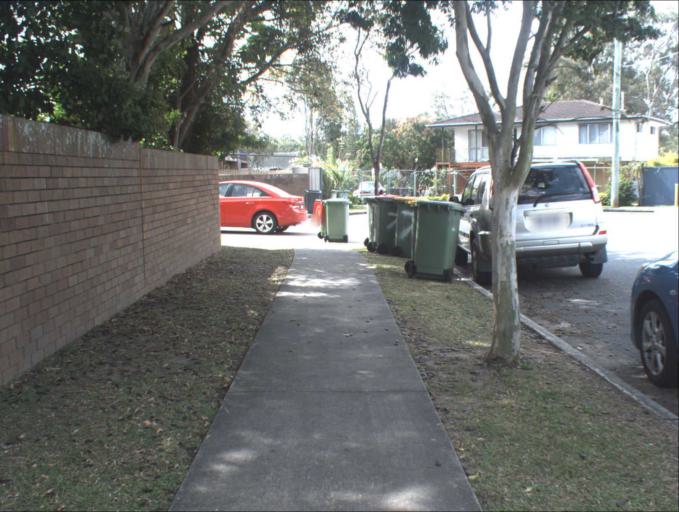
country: AU
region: Queensland
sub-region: Logan
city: Waterford West
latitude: -27.6749
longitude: 153.1292
